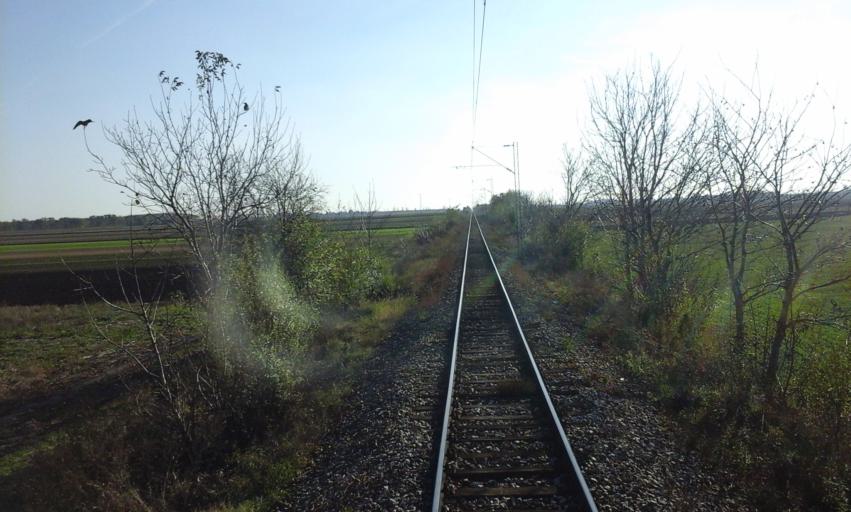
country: RS
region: Autonomna Pokrajina Vojvodina
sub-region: Severnobacki Okrug
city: Backa Topola
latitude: 45.8002
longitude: 19.6472
